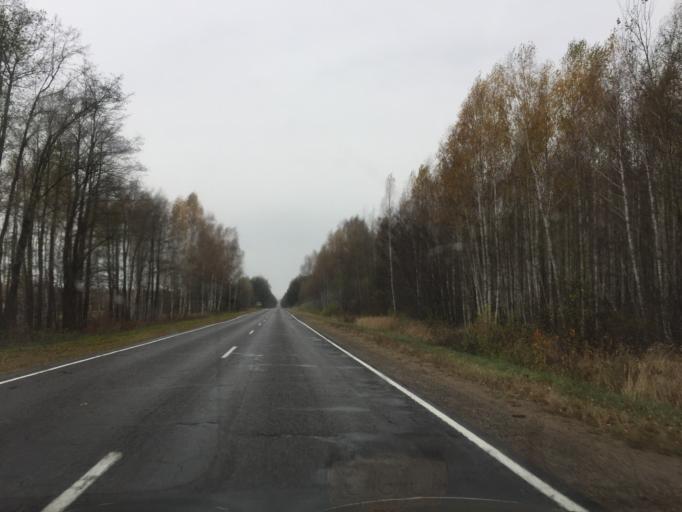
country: BY
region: Gomel
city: Karma
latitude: 53.3241
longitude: 30.7693
